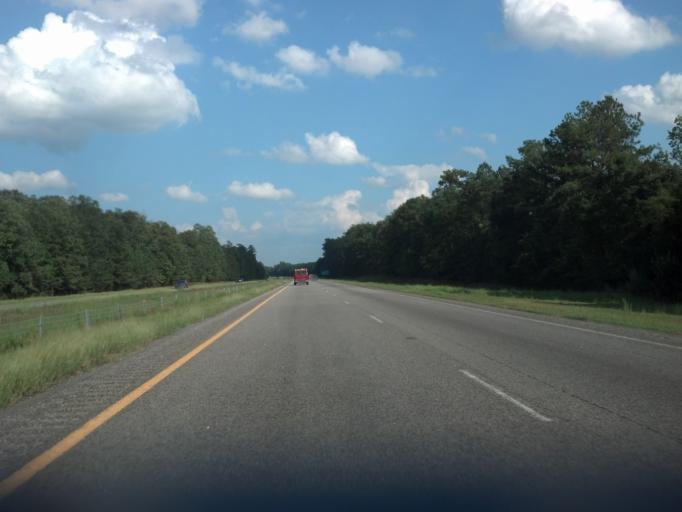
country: US
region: North Carolina
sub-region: Edgecombe County
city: Tarboro
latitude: 35.8920
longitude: -77.6167
